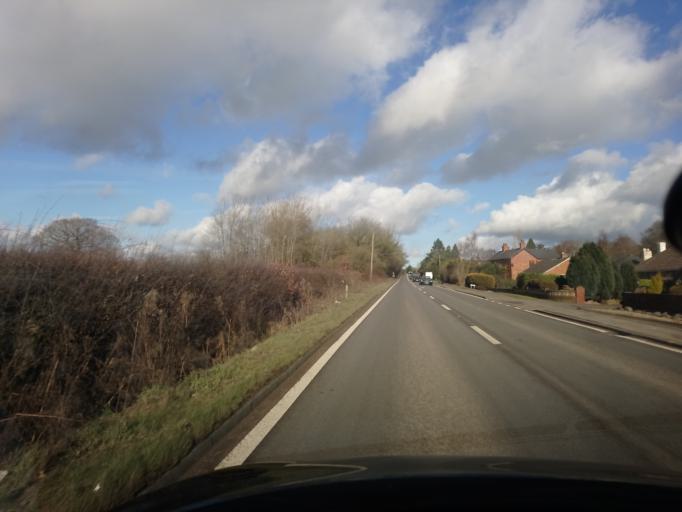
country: GB
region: England
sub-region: Shropshire
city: Astley
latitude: 52.7550
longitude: -2.7165
